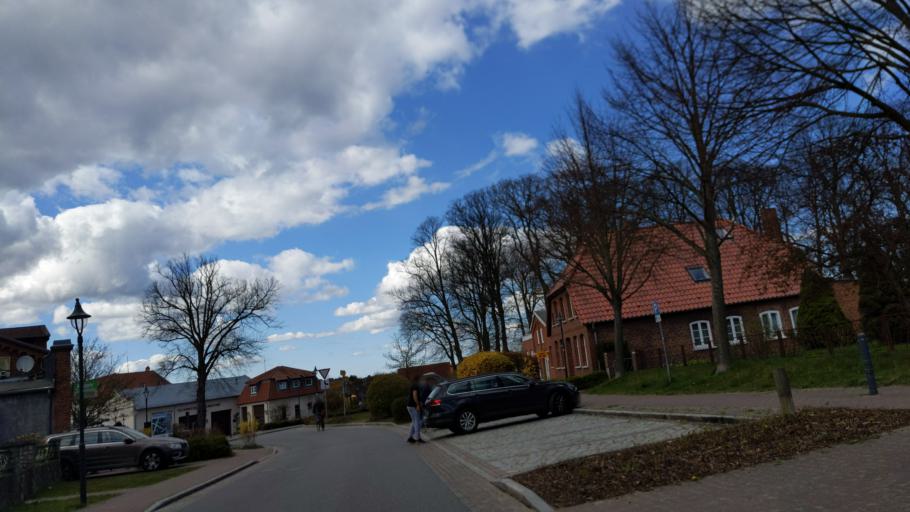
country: DE
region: Mecklenburg-Vorpommern
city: Selmsdorf
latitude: 53.8811
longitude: 10.8605
